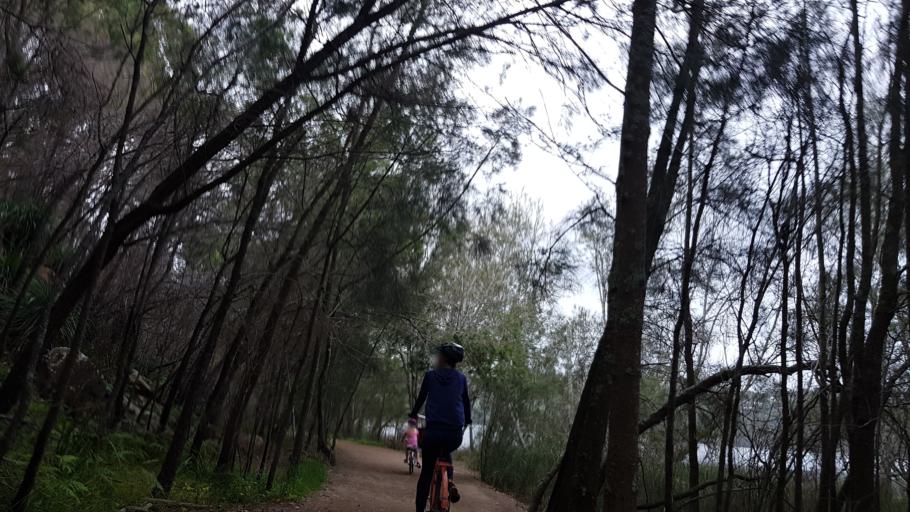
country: AU
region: New South Wales
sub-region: Warringah
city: Narrabeen
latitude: -33.7170
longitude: 151.2846
